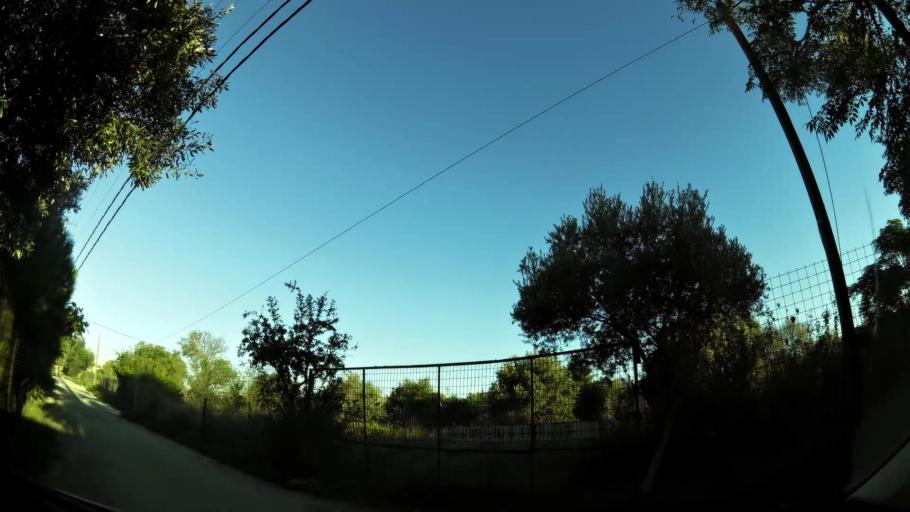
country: GR
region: Attica
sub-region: Nomarchia Anatolikis Attikis
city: Pallini
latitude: 37.9985
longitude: 23.8684
